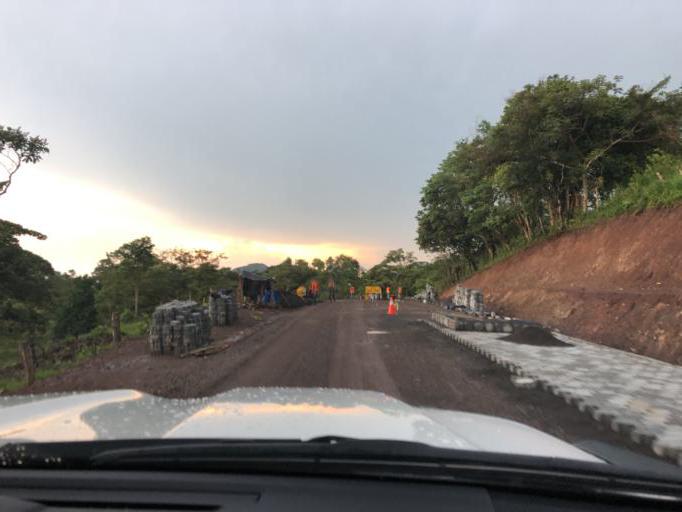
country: NI
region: Chontales
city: La Libertad
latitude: 12.2004
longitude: -85.1767
